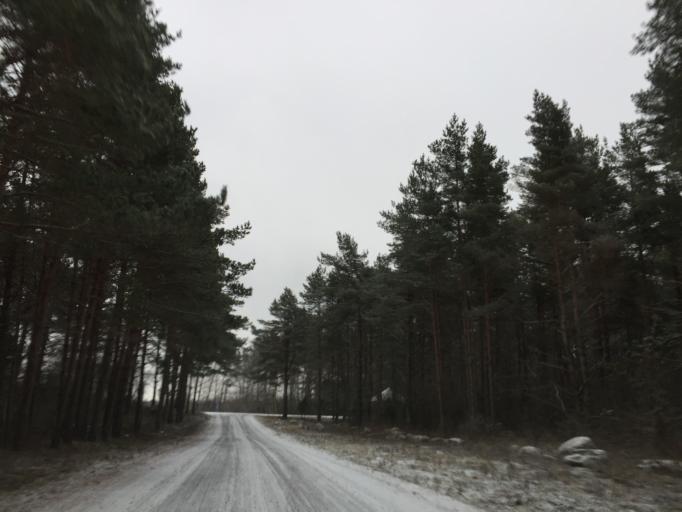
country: EE
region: Saare
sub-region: Orissaare vald
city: Orissaare
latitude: 58.6173
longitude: 23.1929
